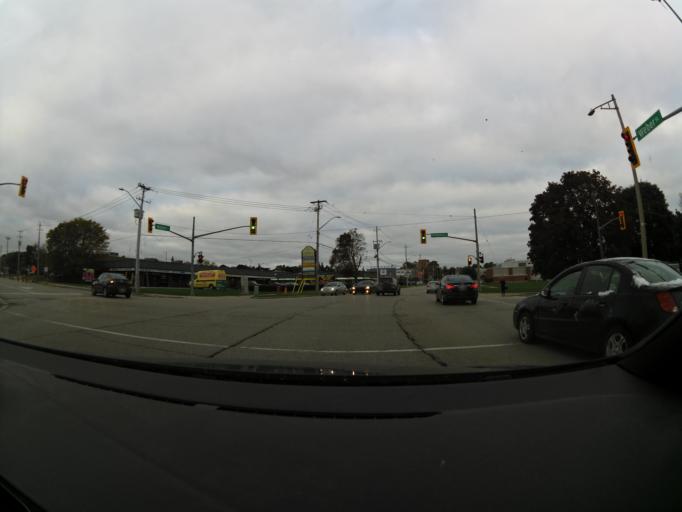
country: CA
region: Ontario
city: Kitchener
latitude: 43.4382
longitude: -80.4583
